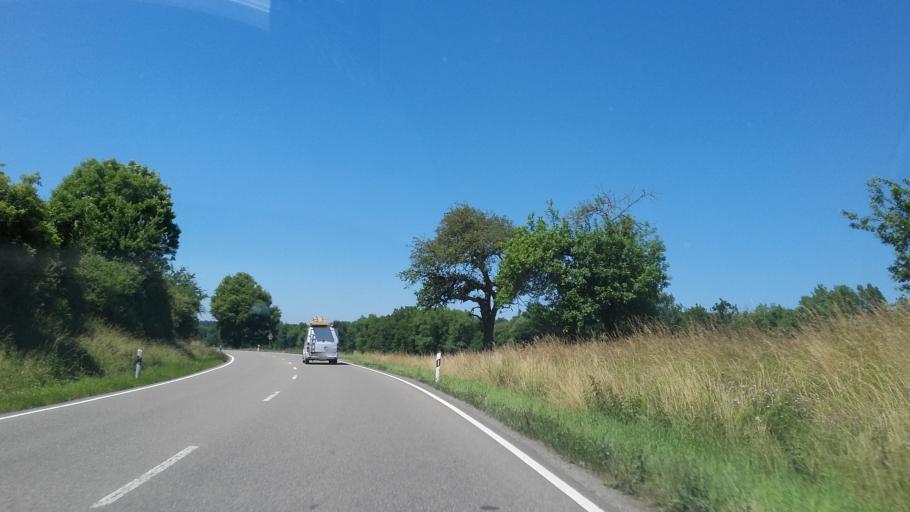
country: DE
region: Baden-Wuerttemberg
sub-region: Karlsruhe Region
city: Illingen
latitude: 48.9602
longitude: 8.9009
